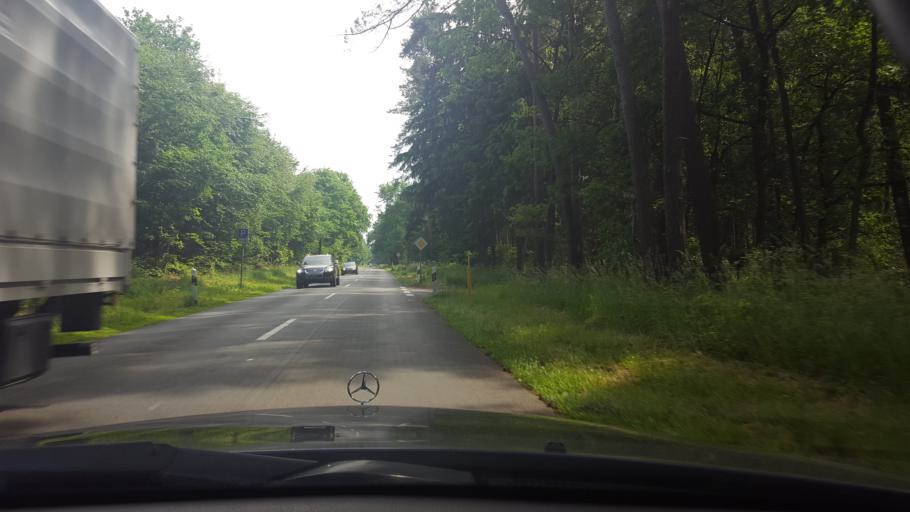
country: DE
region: North Rhine-Westphalia
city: Olfen
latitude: 51.7185
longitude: 7.3068
